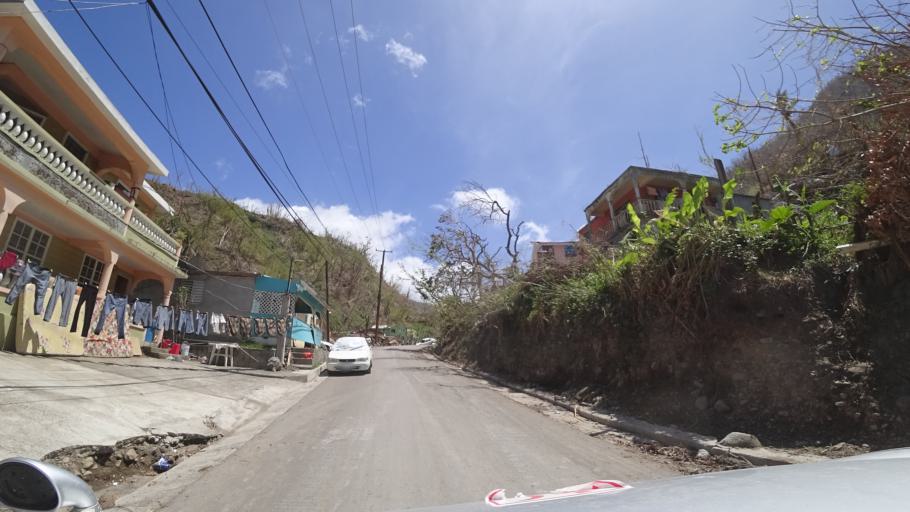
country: DM
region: Saint Luke
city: Pointe Michel
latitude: 15.2756
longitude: -61.3704
